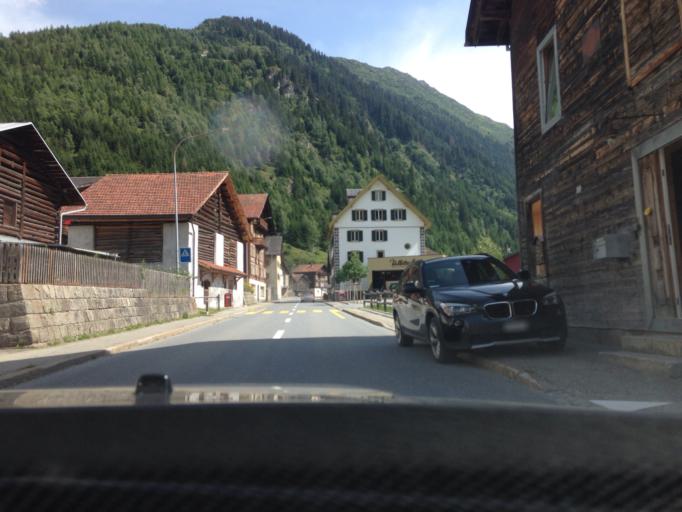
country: CH
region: Grisons
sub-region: Surselva District
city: Disentis
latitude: 46.6740
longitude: 8.8573
